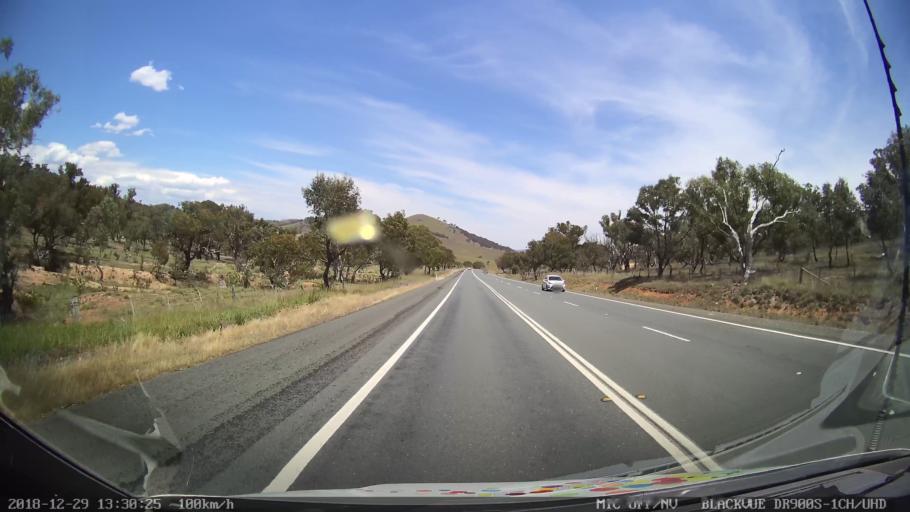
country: AU
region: New South Wales
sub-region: Cooma-Monaro
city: Cooma
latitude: -35.9036
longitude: 149.1607
